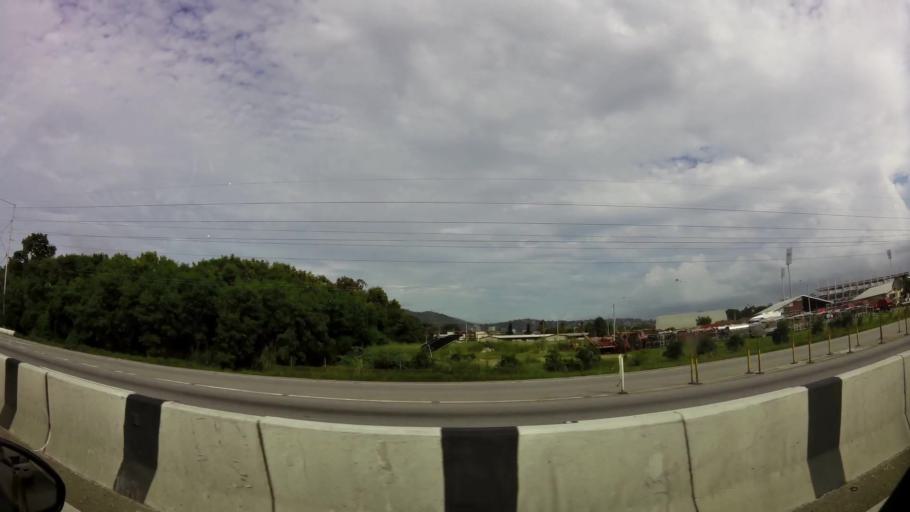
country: TT
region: City of Port of Spain
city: Mucurapo
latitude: 10.6647
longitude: -61.5362
